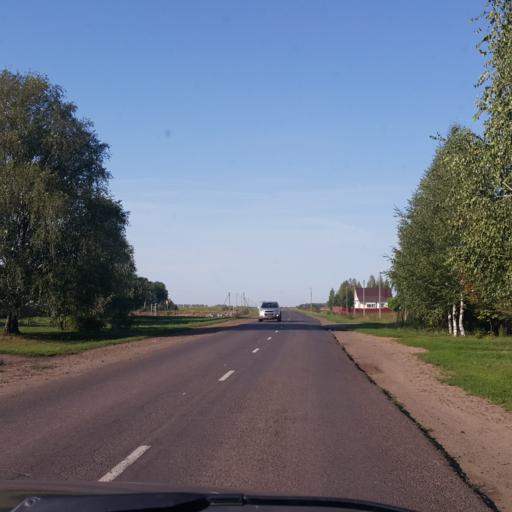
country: RU
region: Tambov
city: Novaya Lyada
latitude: 52.7708
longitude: 41.7459
